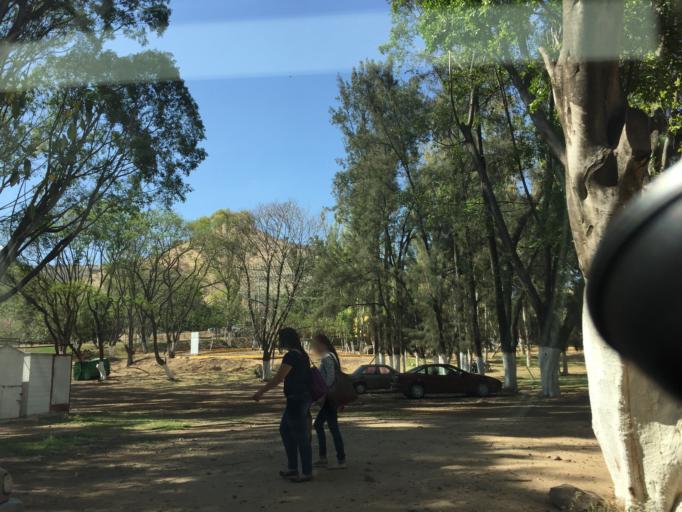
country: MX
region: Jalisco
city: Atotonilco el Alto
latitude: 20.5640
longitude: -102.4782
